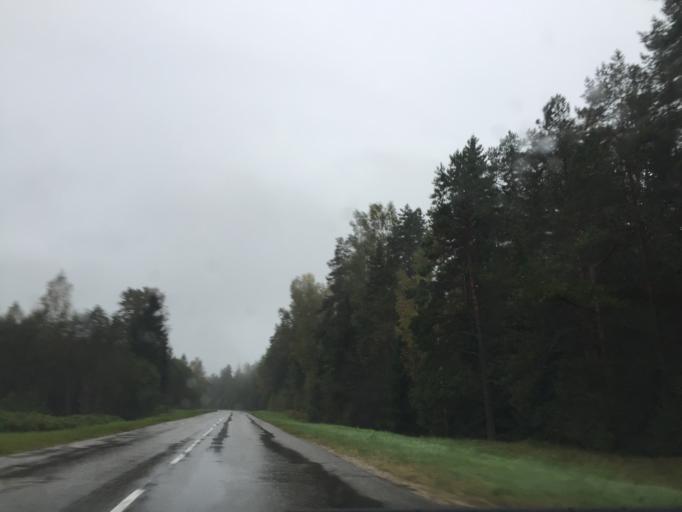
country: LV
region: Incukalns
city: Incukalns
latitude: 57.0286
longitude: 24.6825
